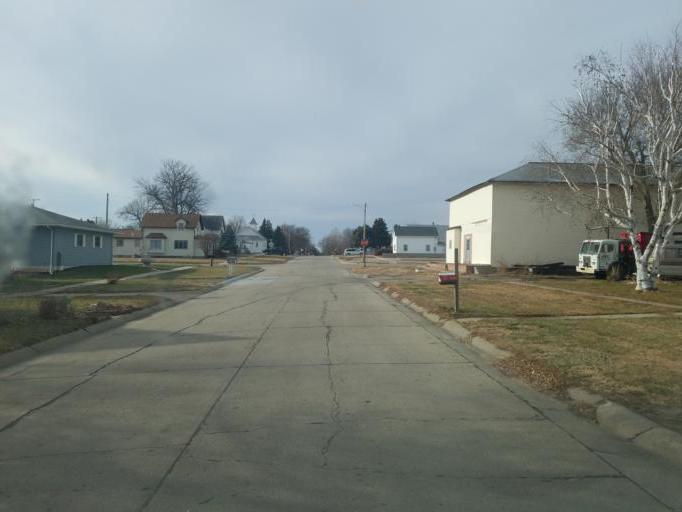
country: US
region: Nebraska
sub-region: Knox County
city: Creighton
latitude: 42.4655
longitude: -97.9041
